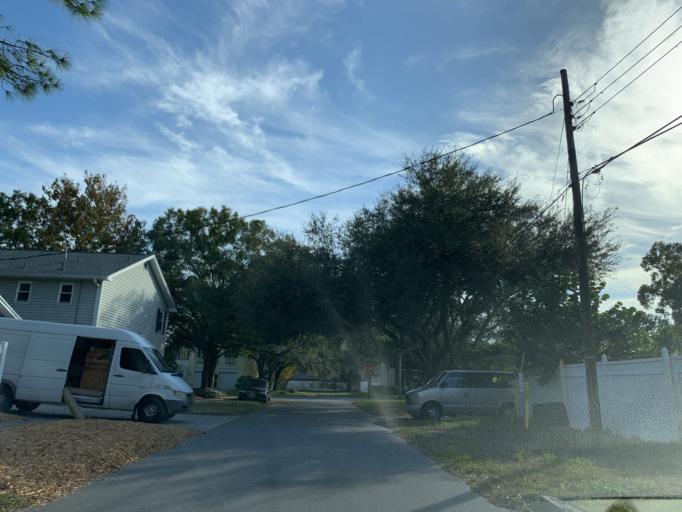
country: US
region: Florida
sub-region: Hillsborough County
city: Tampa
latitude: 27.9020
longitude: -82.5007
